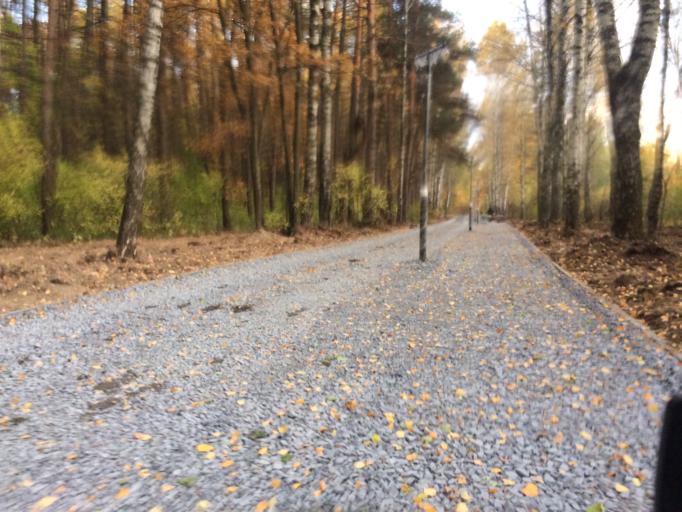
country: RU
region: Mariy-El
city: Yoshkar-Ola
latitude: 56.6251
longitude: 47.9167
